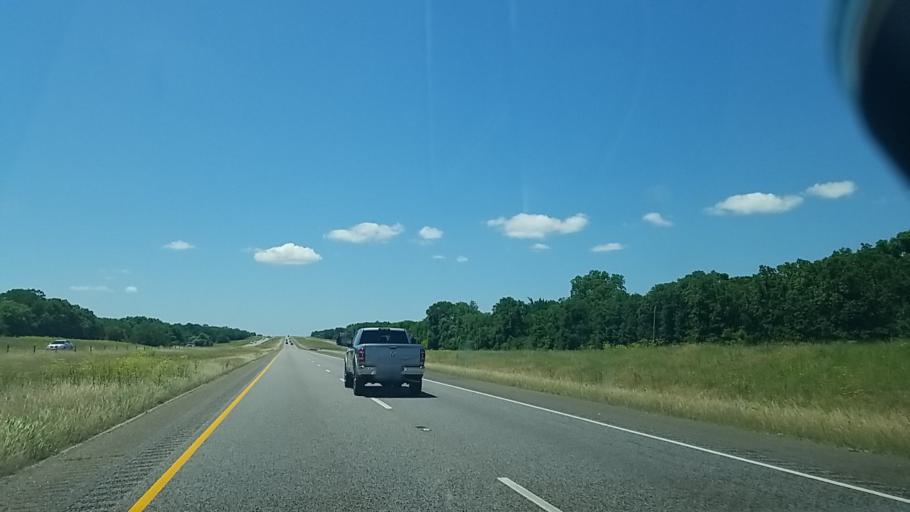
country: US
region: Texas
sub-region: Madison County
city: Madisonville
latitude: 30.9379
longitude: -95.8393
